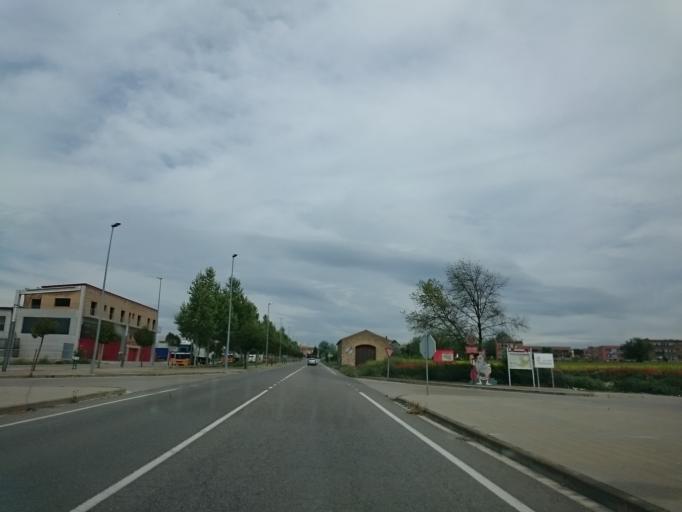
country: ES
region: Catalonia
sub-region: Provincia de Lleida
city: Mont-roig del Camp
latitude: 41.7807
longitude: 1.2790
